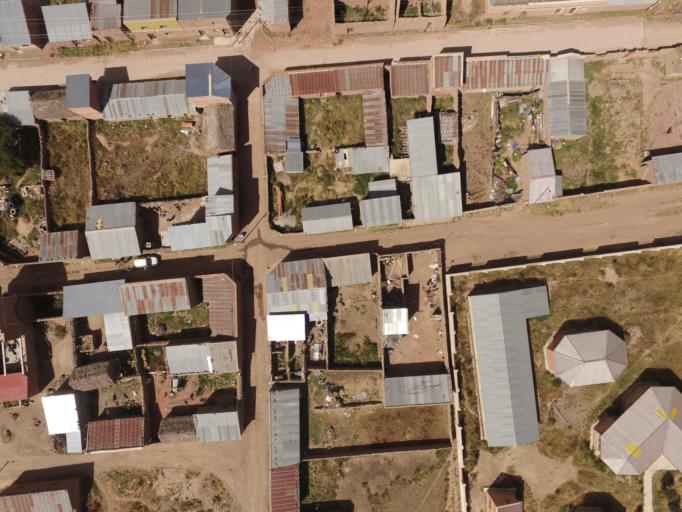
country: BO
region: Oruro
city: Challapata
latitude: -18.6926
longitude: -66.7569
